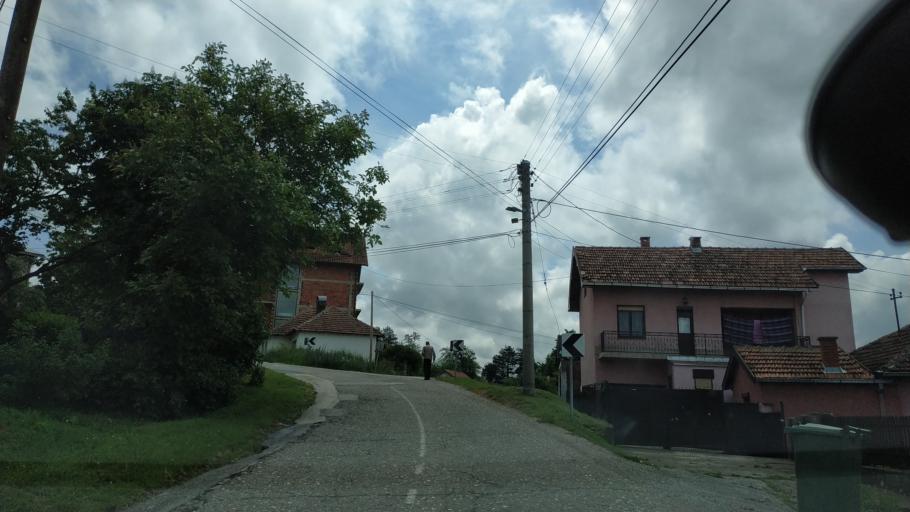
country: RS
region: Central Serbia
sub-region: Zajecarski Okrug
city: Boljevac
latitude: 43.8305
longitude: 21.9634
